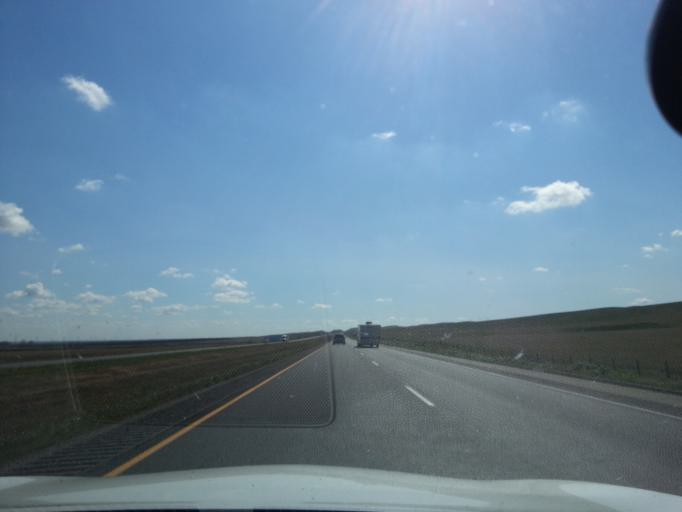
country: US
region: California
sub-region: Fresno County
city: Coalinga
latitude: 36.3461
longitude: -120.3142
